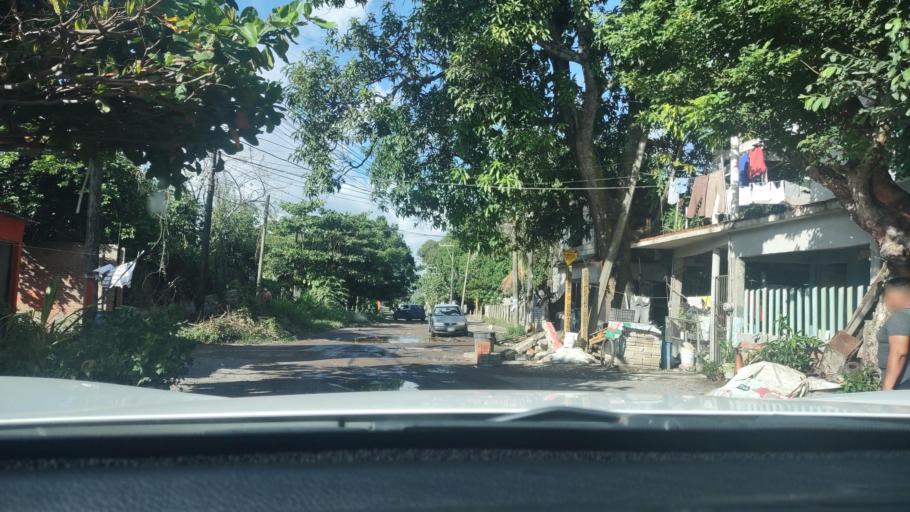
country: MX
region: Veracruz
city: El Tejar
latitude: 19.0707
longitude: -96.1587
